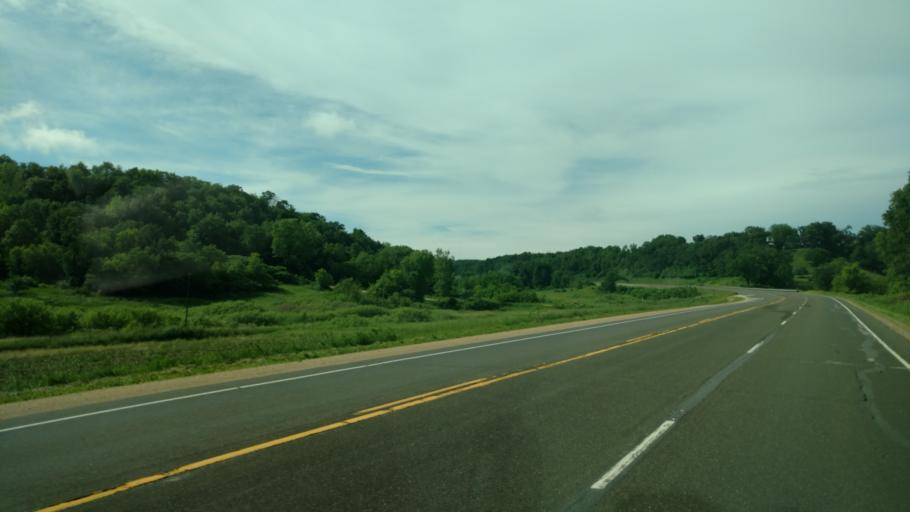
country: US
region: Wisconsin
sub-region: Monroe County
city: Tomah
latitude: 43.8833
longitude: -90.4808
